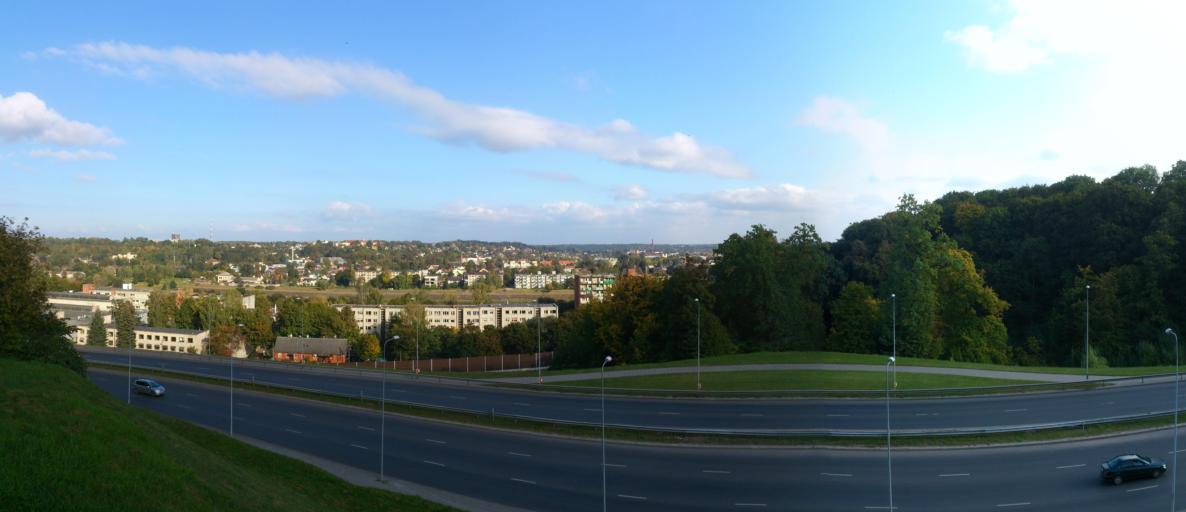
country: LT
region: Kauno apskritis
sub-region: Kaunas
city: Aleksotas
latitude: 54.8748
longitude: 23.9210
